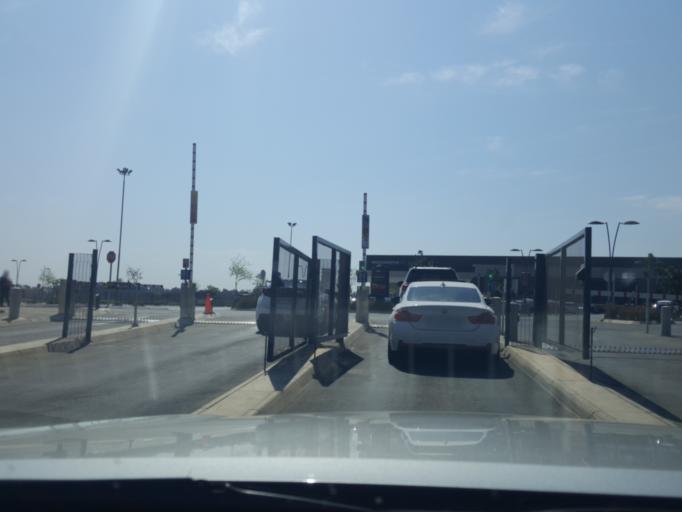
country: ZA
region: Gauteng
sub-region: City of Johannesburg Metropolitan Municipality
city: Midrand
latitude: -25.9836
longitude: 28.0740
